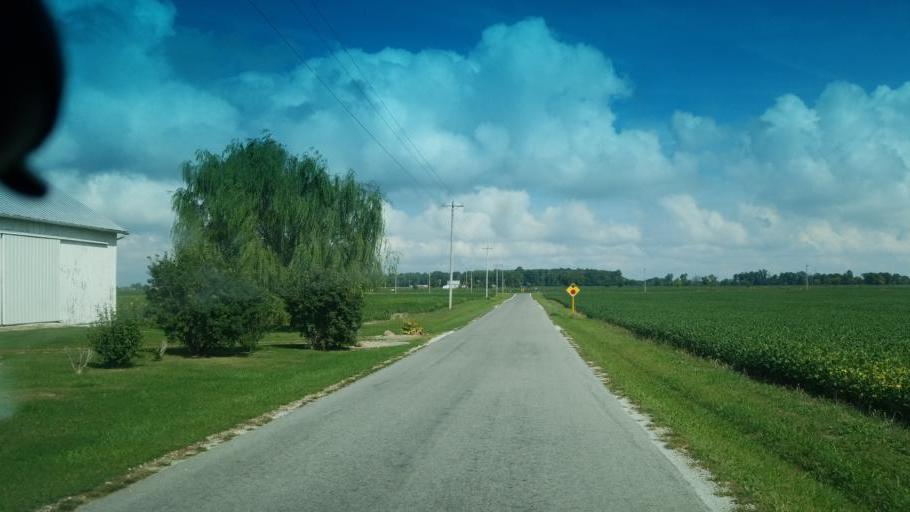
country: US
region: Ohio
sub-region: Wyandot County
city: Carey
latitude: 40.9020
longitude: -83.3992
